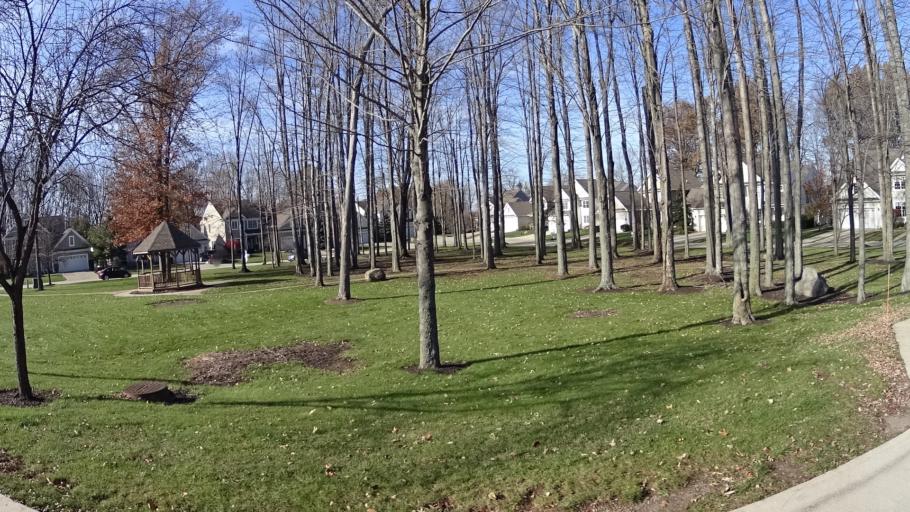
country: US
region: Ohio
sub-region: Lorain County
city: Avon
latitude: 41.4486
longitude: -82.0403
